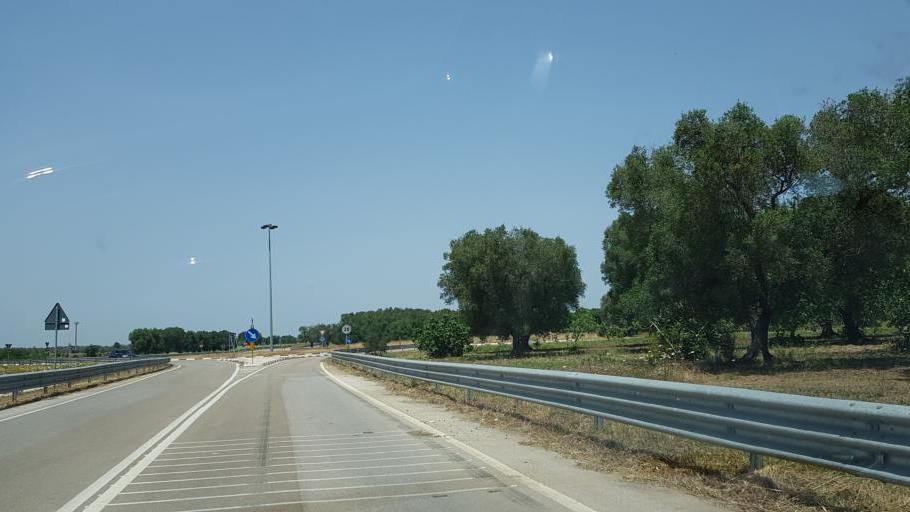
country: IT
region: Apulia
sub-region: Provincia di Brindisi
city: San Pancrazio Salentino
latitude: 40.4846
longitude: 17.8346
